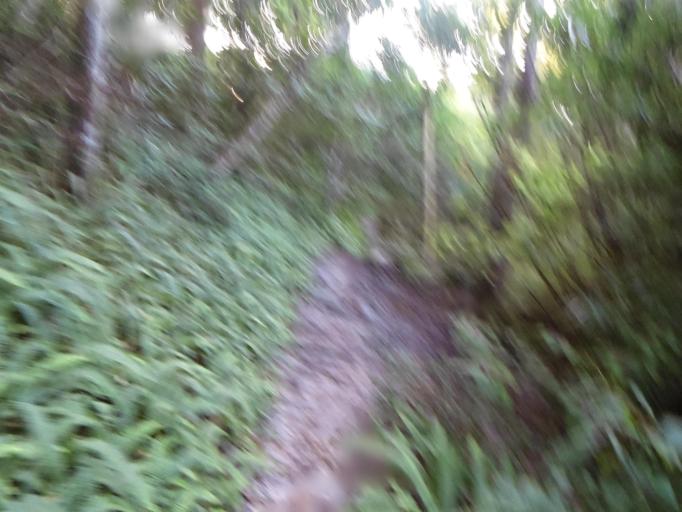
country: US
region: Florida
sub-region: Putnam County
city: Palatka
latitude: 29.6351
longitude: -81.6492
